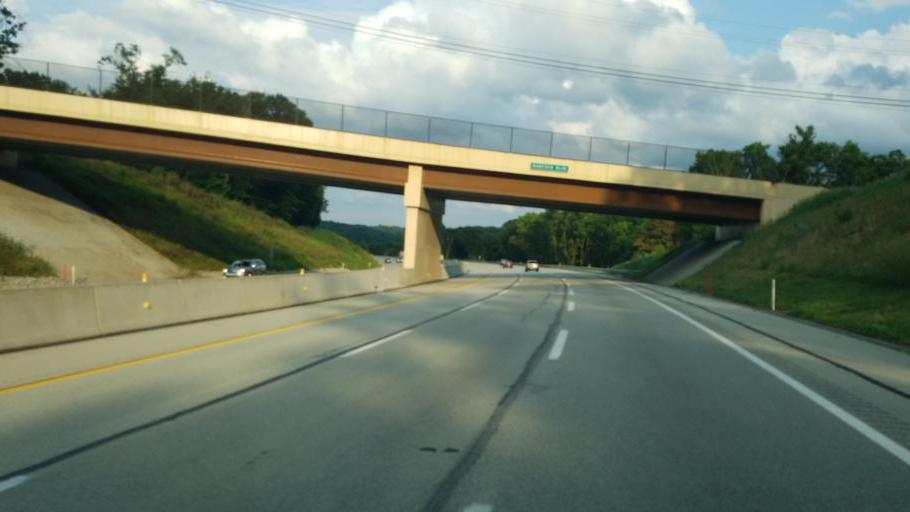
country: US
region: Pennsylvania
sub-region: Allegheny County
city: Gibsonia
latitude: 40.6405
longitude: -80.0097
